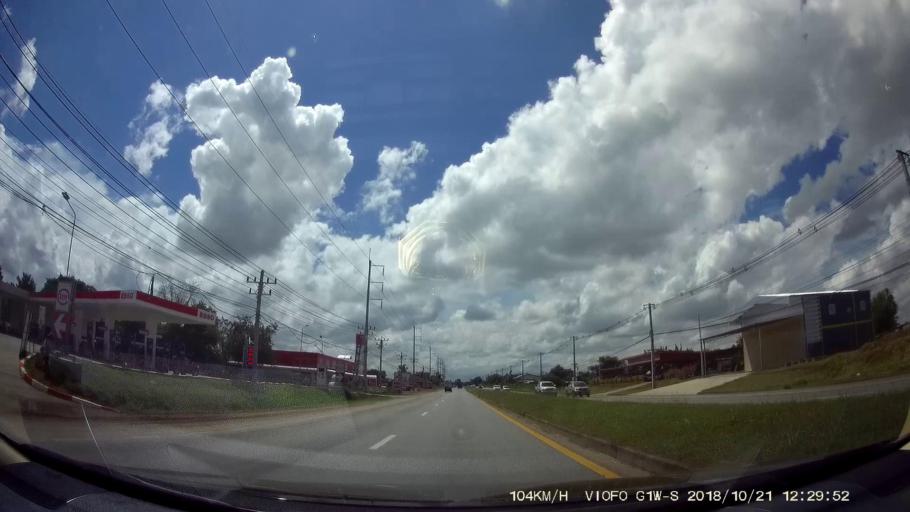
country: TH
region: Nakhon Ratchasima
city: Dan Khun Thot
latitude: 15.1774
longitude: 101.7445
